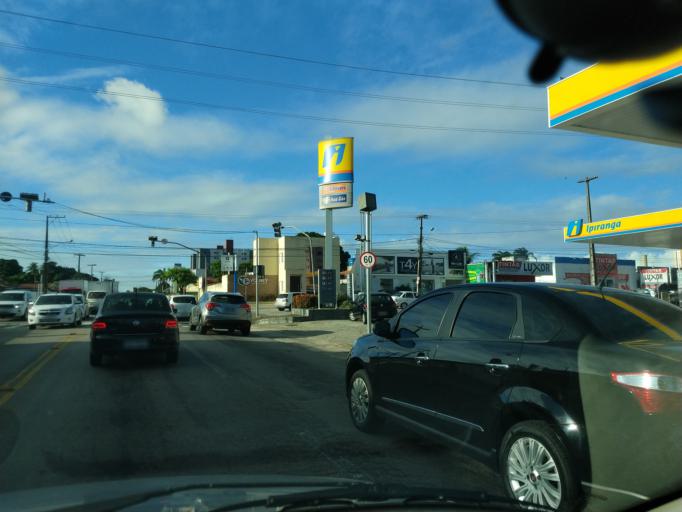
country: BR
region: Rio Grande do Norte
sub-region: Natal
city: Natal
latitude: -5.8176
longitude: -35.2179
